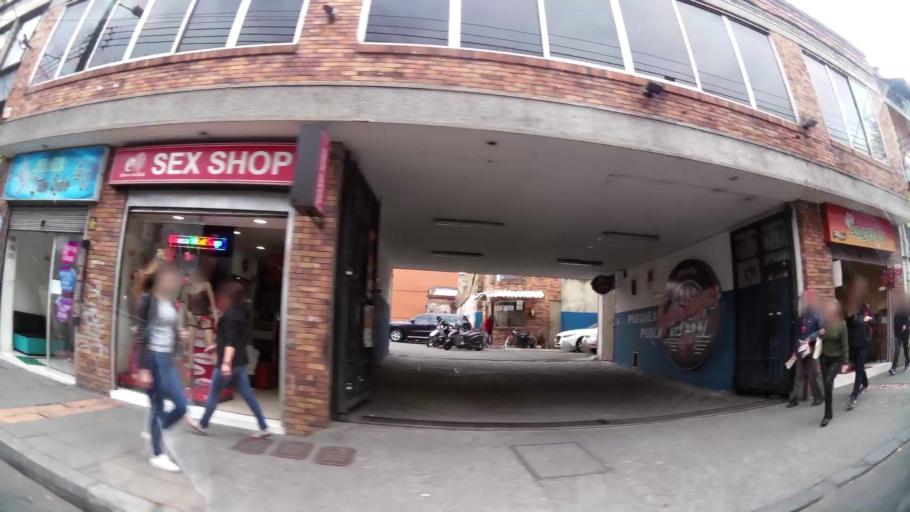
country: CO
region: Bogota D.C.
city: Bogota
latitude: 4.6461
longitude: -74.0626
